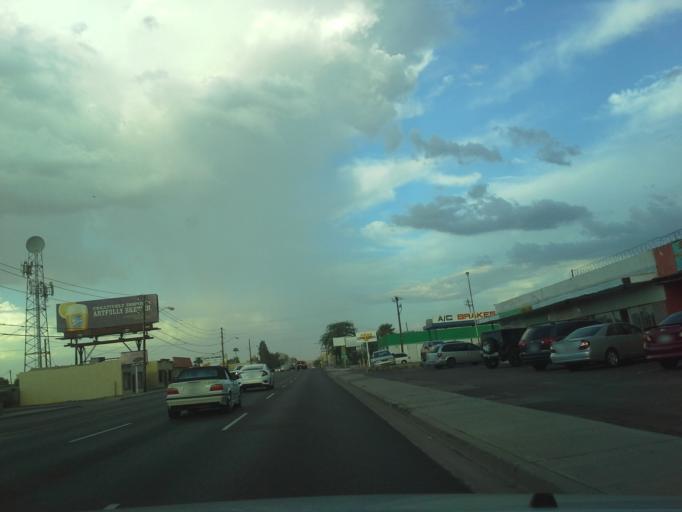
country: US
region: Arizona
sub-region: Maricopa County
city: Phoenix
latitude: 33.4657
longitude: -112.0183
